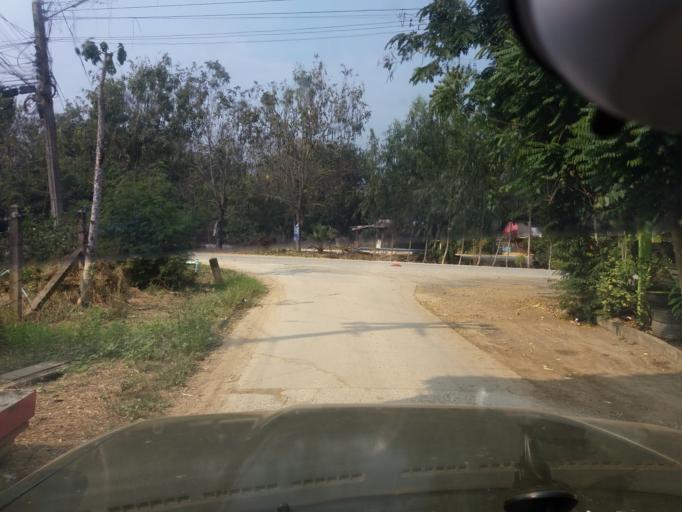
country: TH
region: Suphan Buri
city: Doem Bang Nang Buat
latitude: 14.8952
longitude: 100.2037
